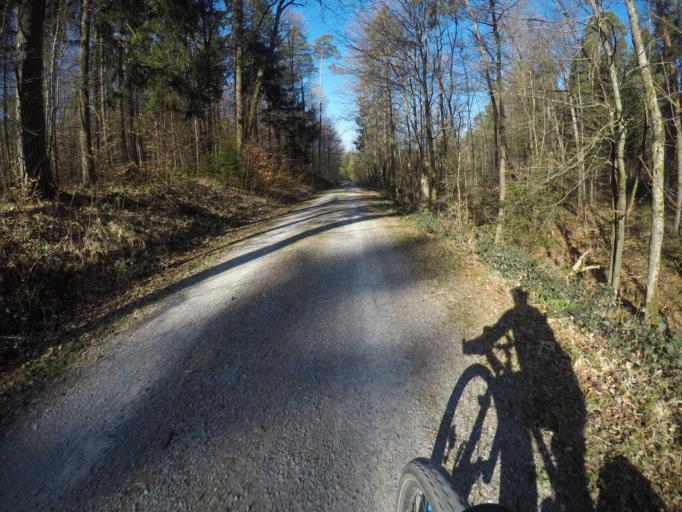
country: DE
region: Baden-Wuerttemberg
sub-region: Tuebingen Region
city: Dettenhausen
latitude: 48.6070
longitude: 9.1168
